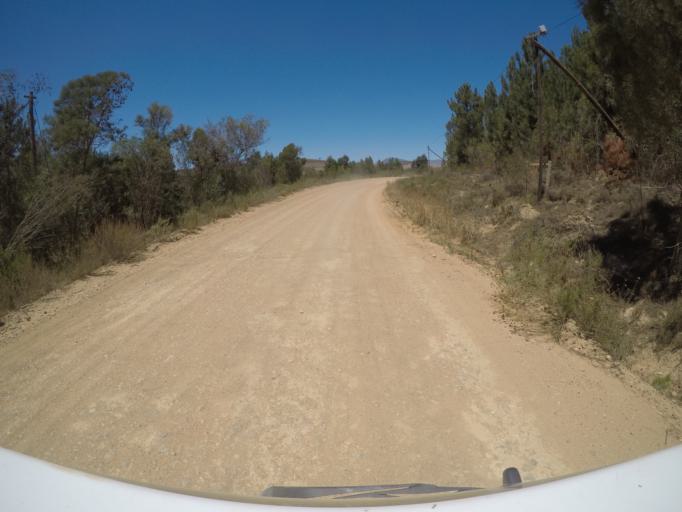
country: ZA
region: Western Cape
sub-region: Overberg District Municipality
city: Caledon
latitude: -34.1868
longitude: 19.2242
